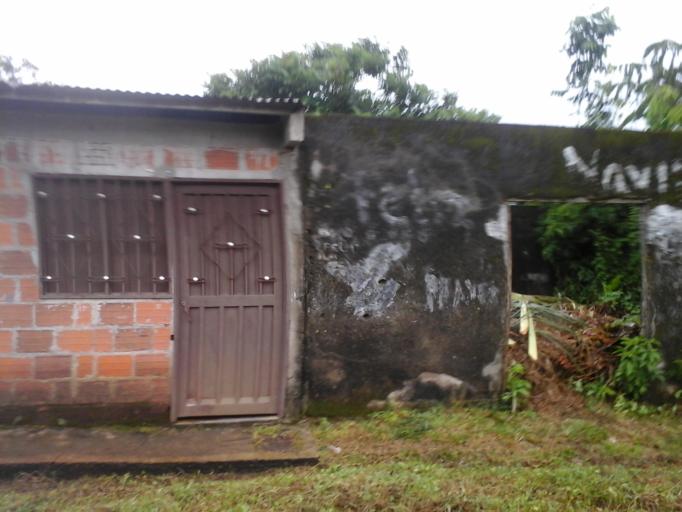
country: CO
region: Caqueta
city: El Doncello
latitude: 1.6117
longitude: -74.9962
